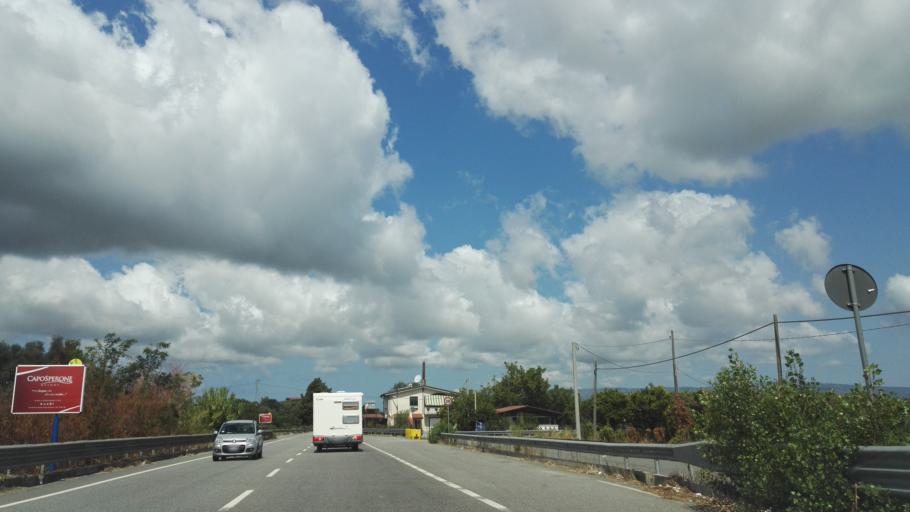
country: IT
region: Calabria
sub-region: Provincia di Reggio Calabria
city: Melicucco
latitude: 38.4575
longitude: 16.0220
